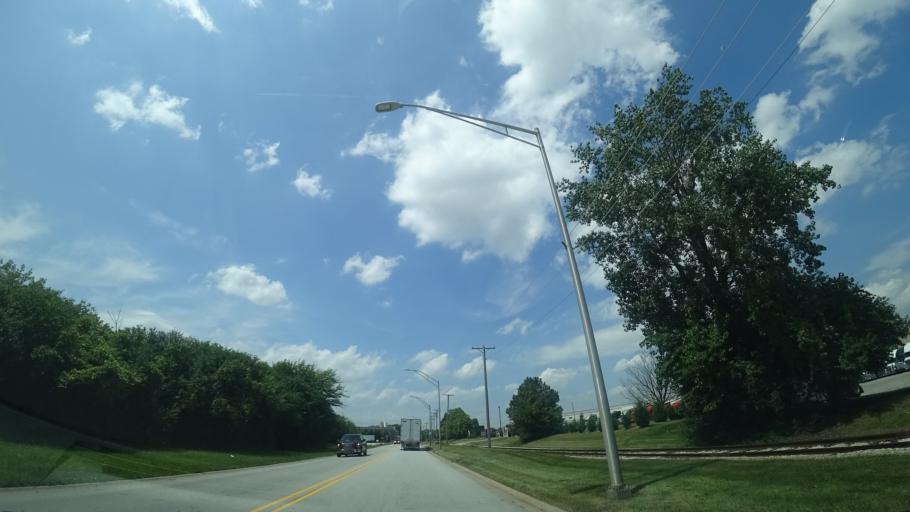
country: US
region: Illinois
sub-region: Cook County
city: Crestwood
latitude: 41.6710
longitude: -87.7559
